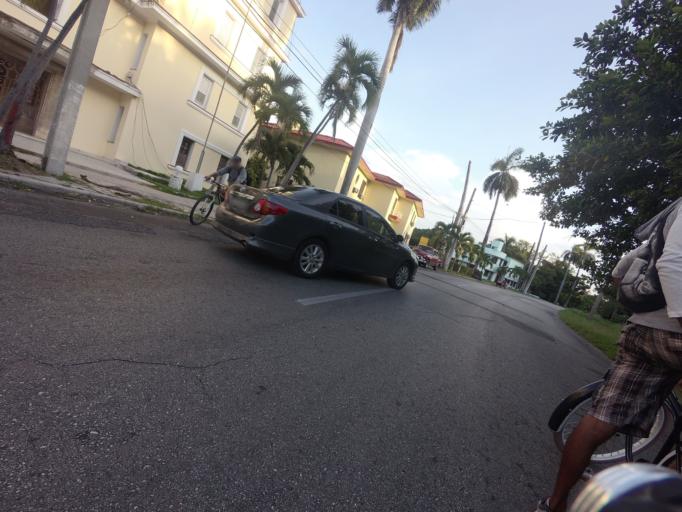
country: CU
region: La Habana
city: Havana
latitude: 23.1225
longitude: -82.4122
